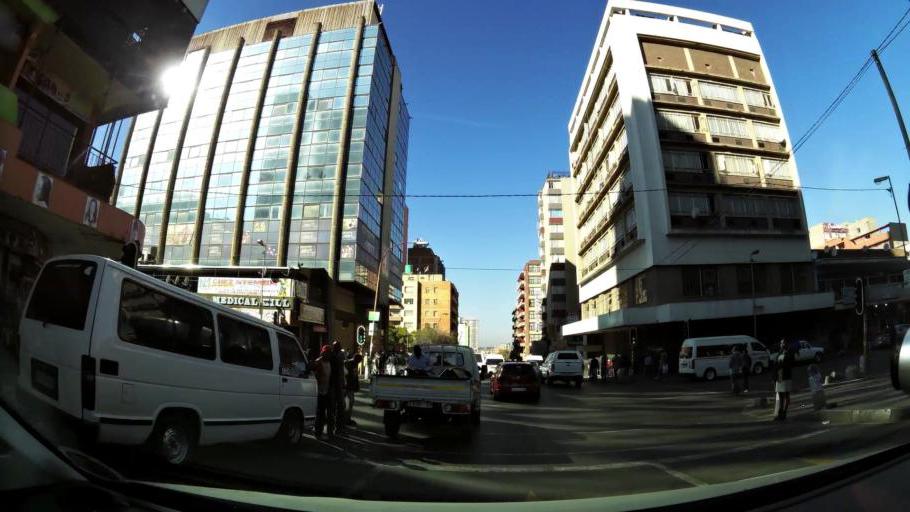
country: ZA
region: Gauteng
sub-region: City of Johannesburg Metropolitan Municipality
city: Johannesburg
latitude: -26.1895
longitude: 28.0492
